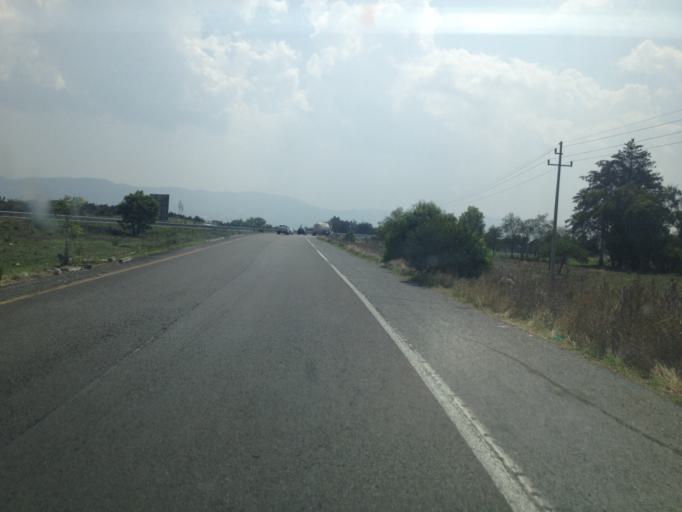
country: MX
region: Puebla
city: Cuacnopalan
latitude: 18.8284
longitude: -97.4916
